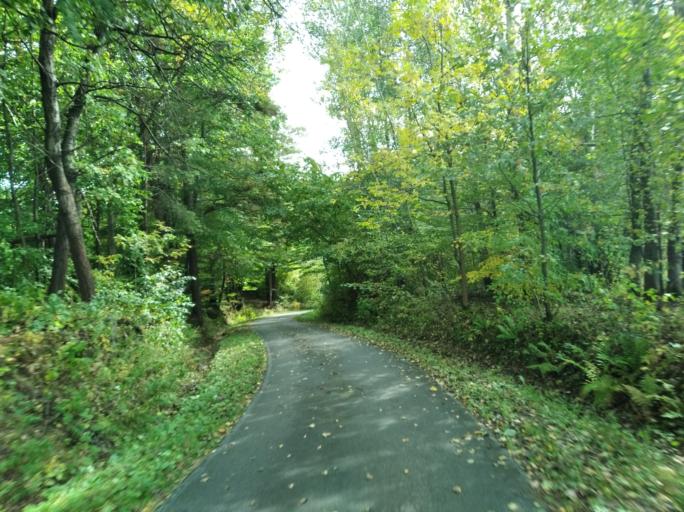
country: PL
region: Subcarpathian Voivodeship
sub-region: Powiat strzyzowski
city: Jawornik
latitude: 49.8342
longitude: 21.8934
